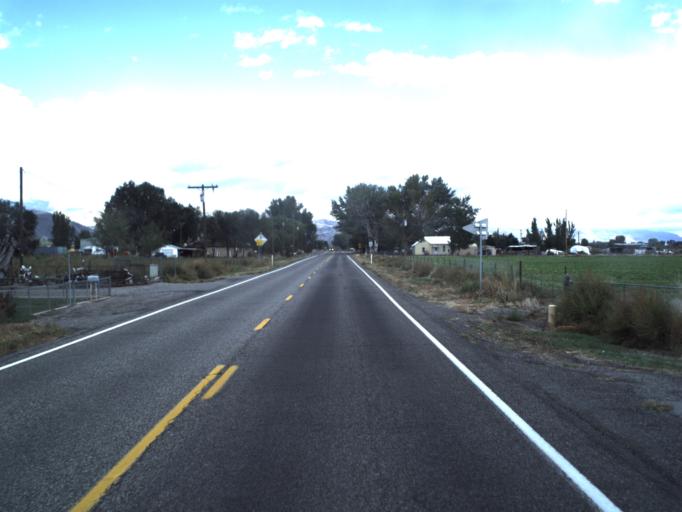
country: US
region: Utah
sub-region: Sevier County
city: Monroe
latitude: 38.6674
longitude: -112.1209
